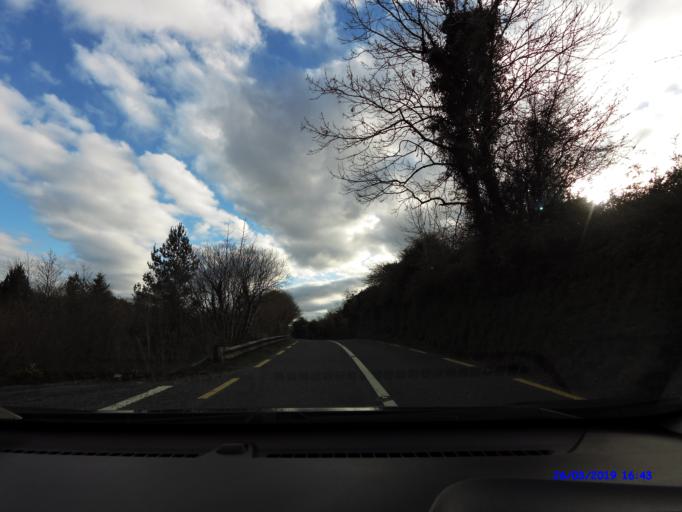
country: IE
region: Connaught
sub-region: Maigh Eo
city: Ballyhaunis
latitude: 53.8604
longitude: -8.7651
